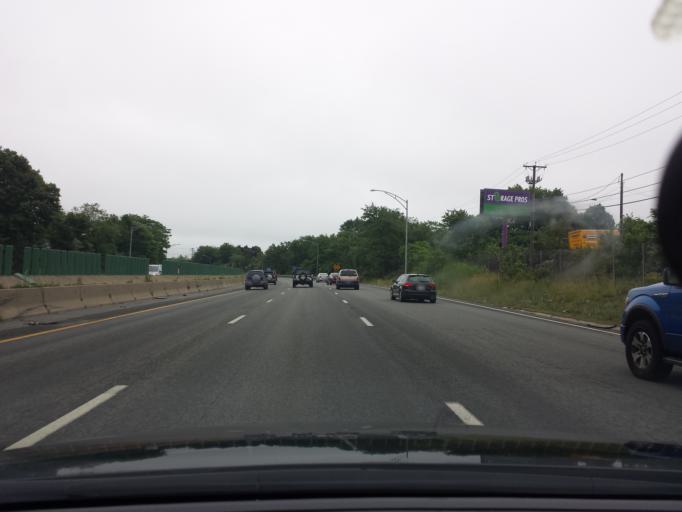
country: US
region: Massachusetts
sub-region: Bristol County
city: Fall River
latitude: 41.6837
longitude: -71.1346
